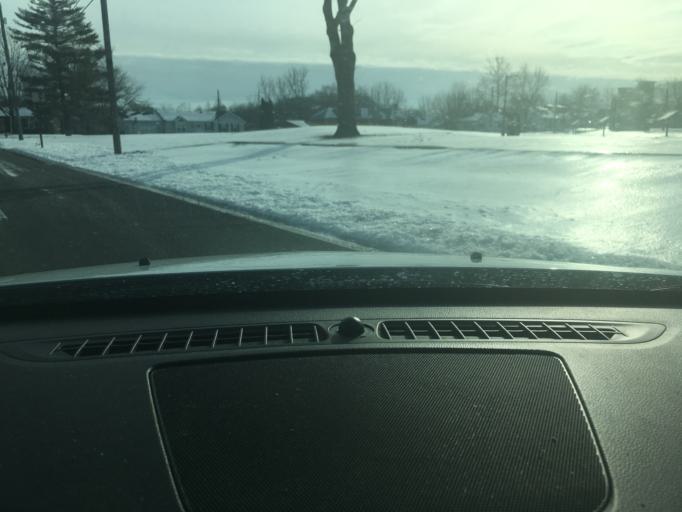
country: US
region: Illinois
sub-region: LaSalle County
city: Peru
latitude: 41.3335
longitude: -89.1221
